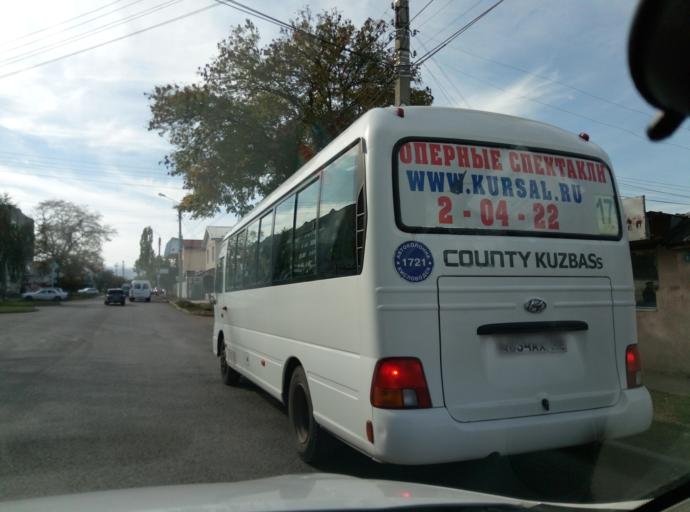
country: RU
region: Stavropol'skiy
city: Kislovodsk
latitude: 43.9275
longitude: 42.7111
